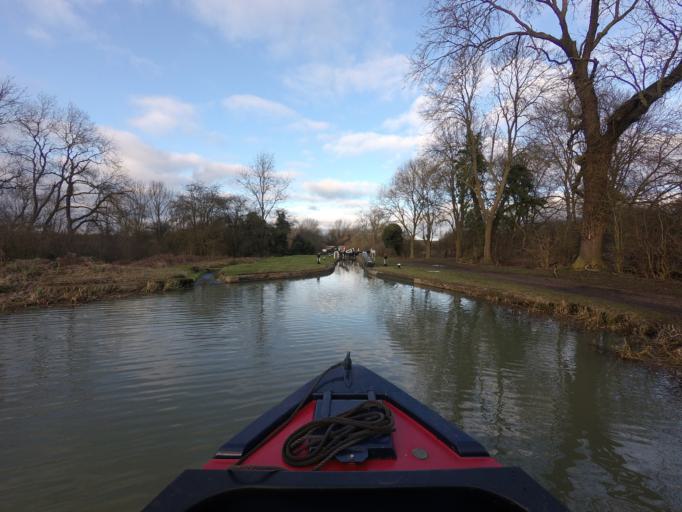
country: GB
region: England
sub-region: Northamptonshire
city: Blisworth
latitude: 52.2053
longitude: -0.9389
